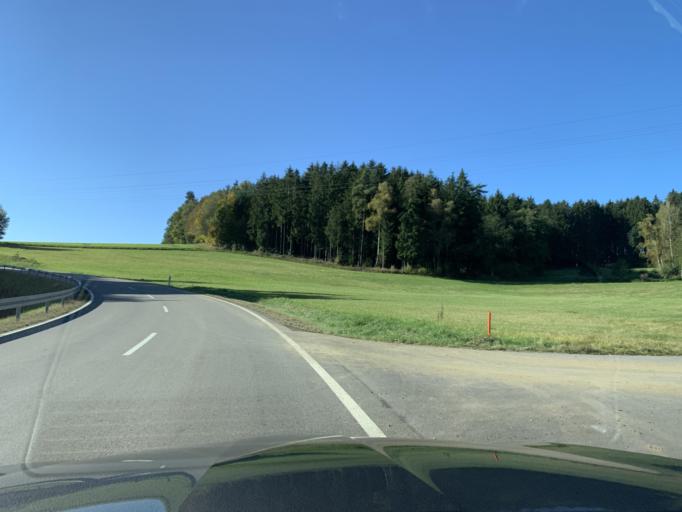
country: DE
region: Bavaria
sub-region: Upper Palatinate
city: Winklarn
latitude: 49.4159
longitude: 12.4670
